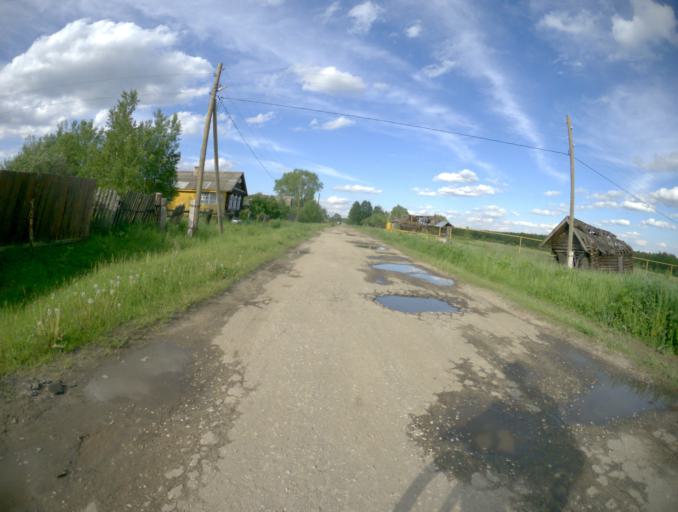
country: RU
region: Vladimir
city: Velikodvorskiy
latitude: 55.3729
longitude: 40.8586
